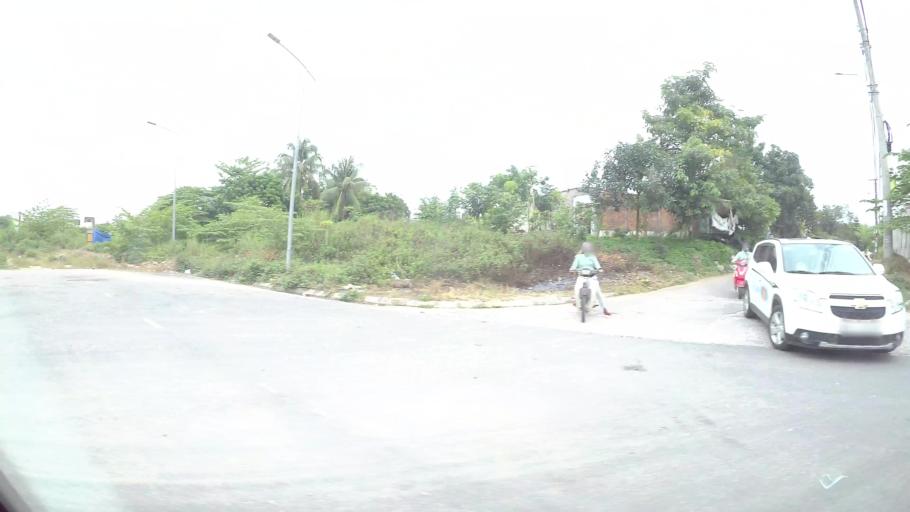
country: VN
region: Da Nang
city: Lien Chieu
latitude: 16.0759
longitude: 108.1568
